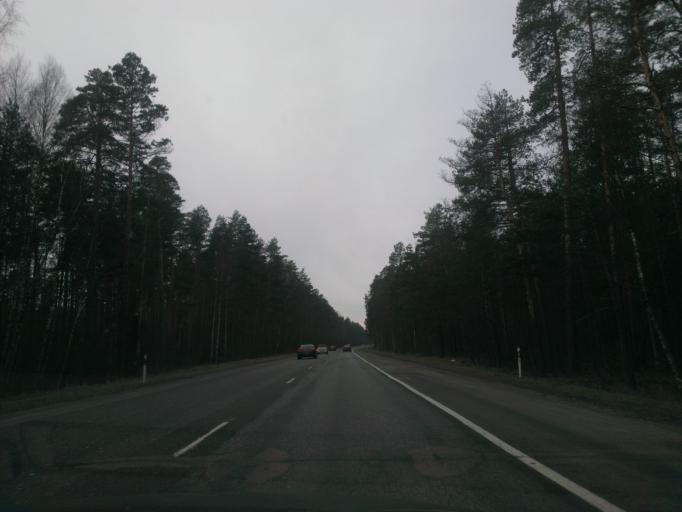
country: LV
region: Incukalns
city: Vangazi
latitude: 57.0754
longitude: 24.5057
